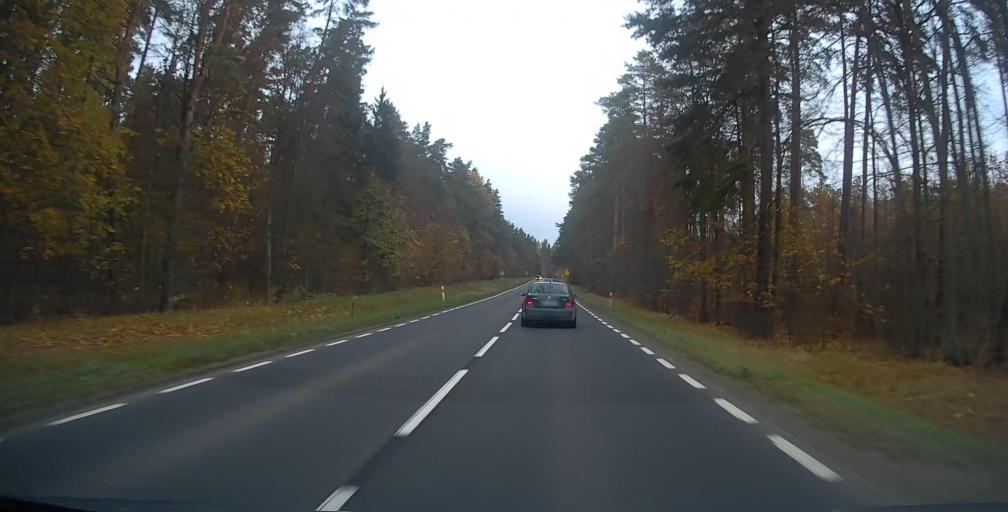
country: PL
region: Warmian-Masurian Voivodeship
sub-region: Powiat elcki
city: Elk
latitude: 53.7894
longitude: 22.3531
